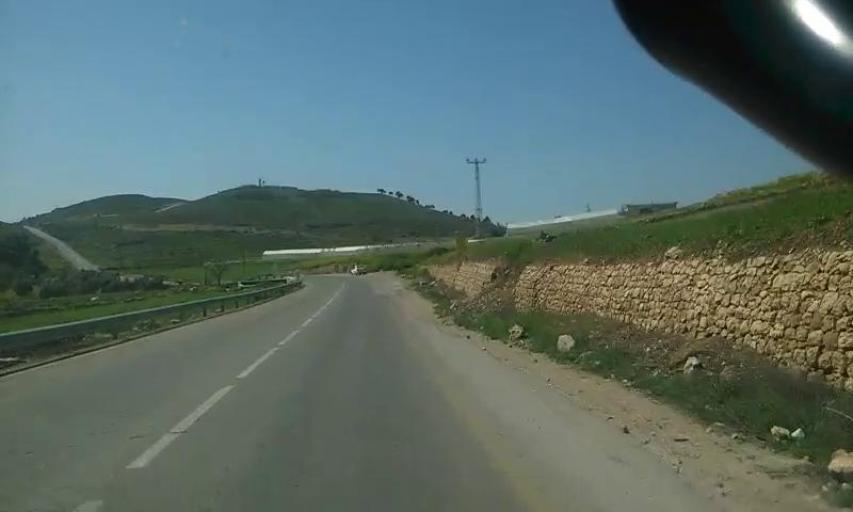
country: PS
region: West Bank
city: Ar Rihiyah
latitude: 31.4833
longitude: 35.0499
